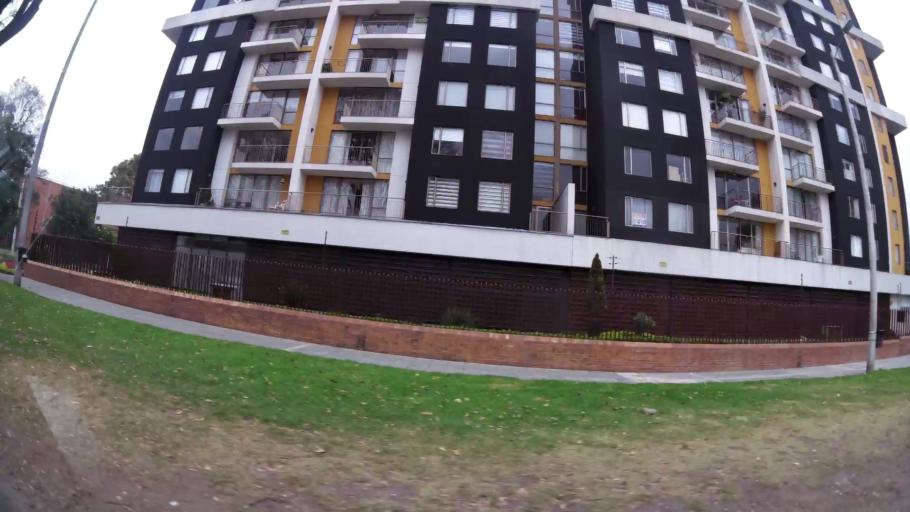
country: CO
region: Bogota D.C.
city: Bogota
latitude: 4.6727
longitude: -74.1185
